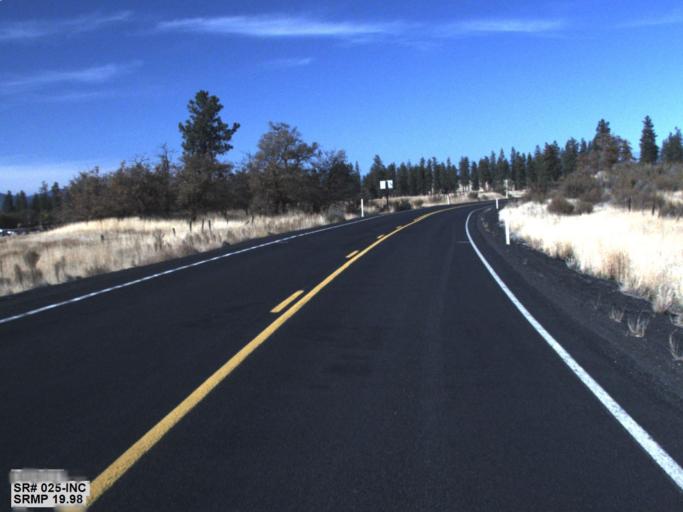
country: US
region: Washington
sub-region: Lincoln County
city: Davenport
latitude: 47.8937
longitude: -118.2723
